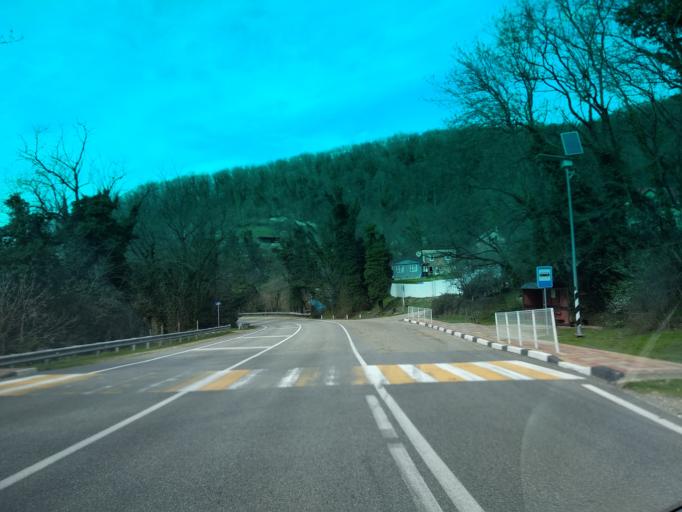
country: RU
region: Krasnodarskiy
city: Shepsi
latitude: 44.0814
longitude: 39.1329
